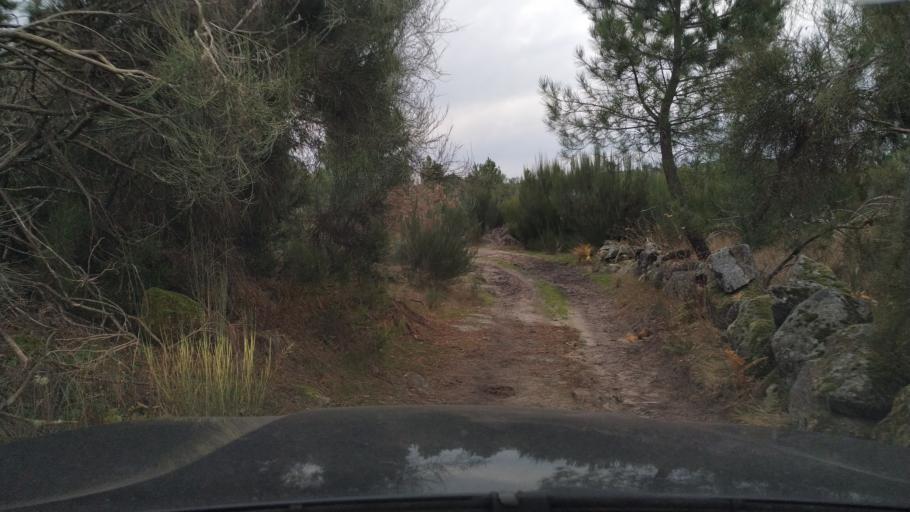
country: PT
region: Vila Real
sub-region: Sabrosa
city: Sabrosa
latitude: 41.3379
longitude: -7.6299
